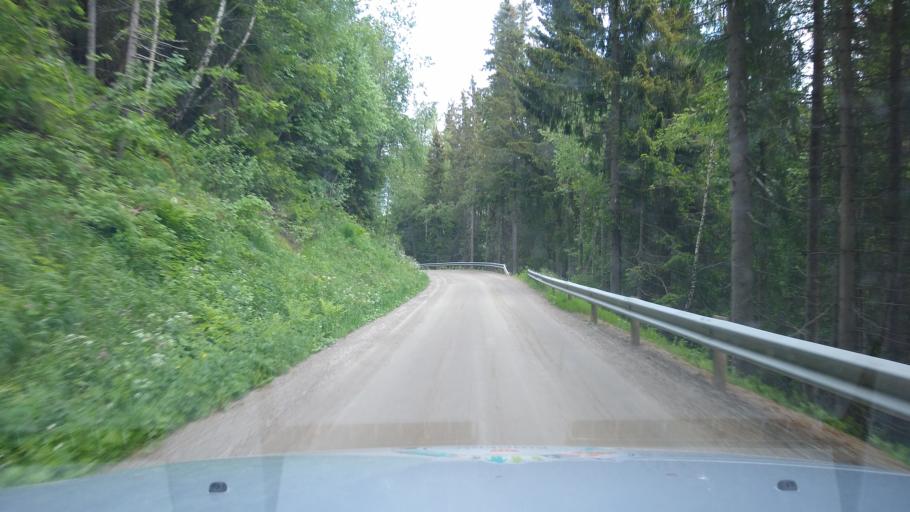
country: NO
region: Oppland
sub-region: Ringebu
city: Ringebu
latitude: 61.5031
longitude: 10.1388
